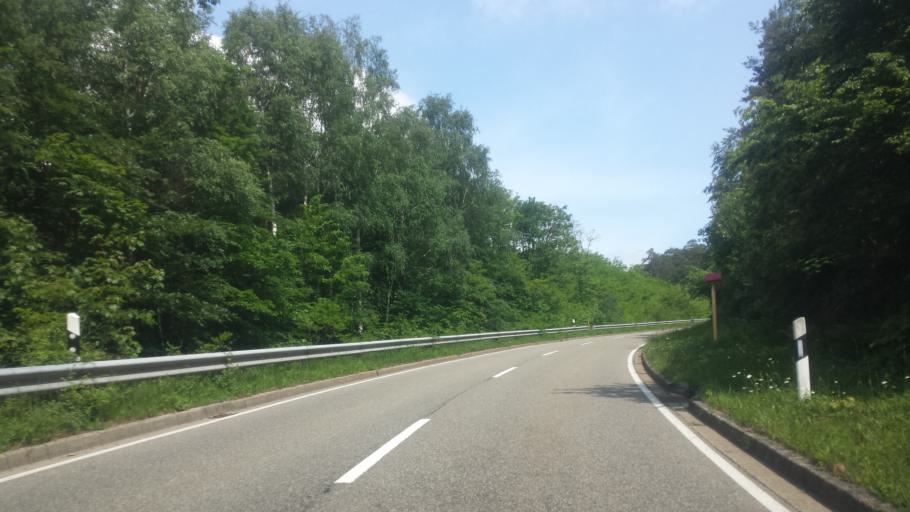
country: DE
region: Rheinland-Pfalz
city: Lindenberg
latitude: 49.3822
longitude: 8.1015
